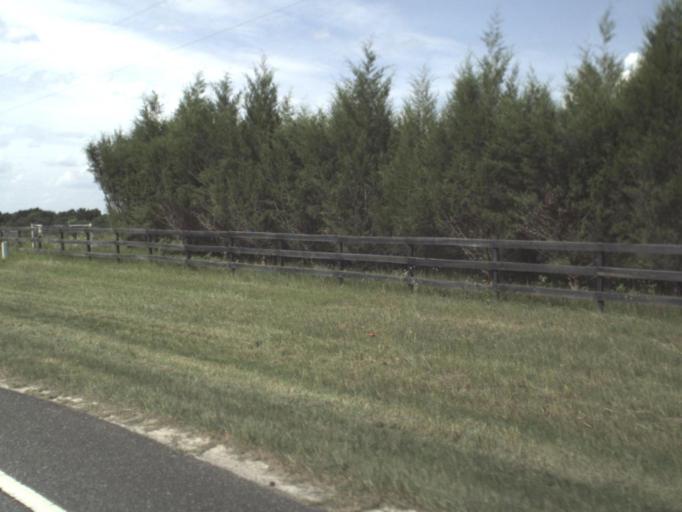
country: US
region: Florida
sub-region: Alachua County
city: High Springs
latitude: 29.9889
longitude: -82.7100
